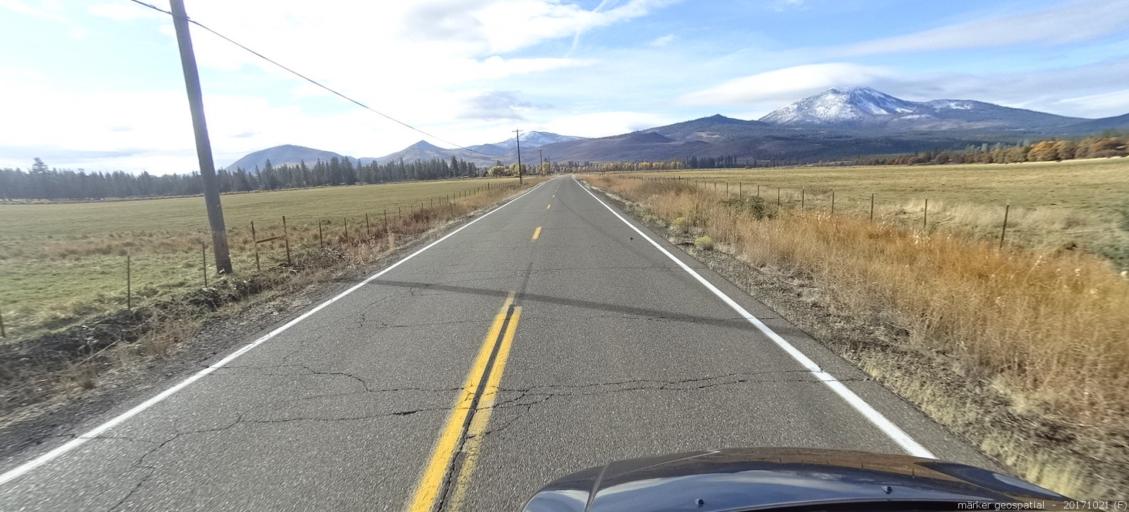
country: US
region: California
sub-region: Shasta County
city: Burney
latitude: 40.8889
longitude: -121.5562
